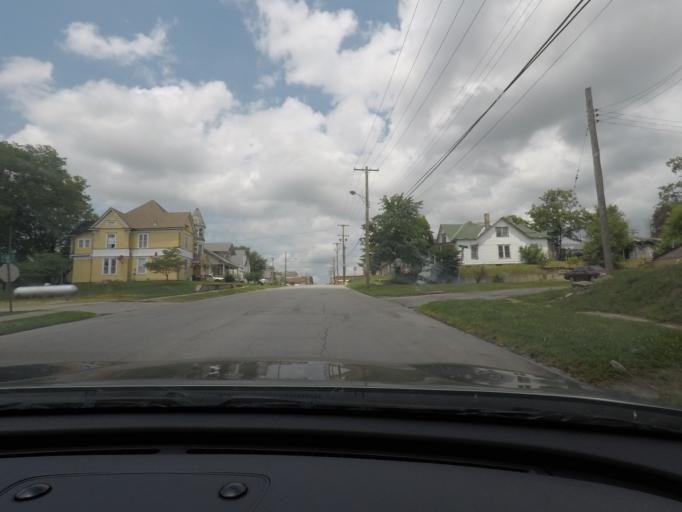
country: US
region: Missouri
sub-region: Carroll County
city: Carrollton
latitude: 39.3546
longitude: -93.4960
